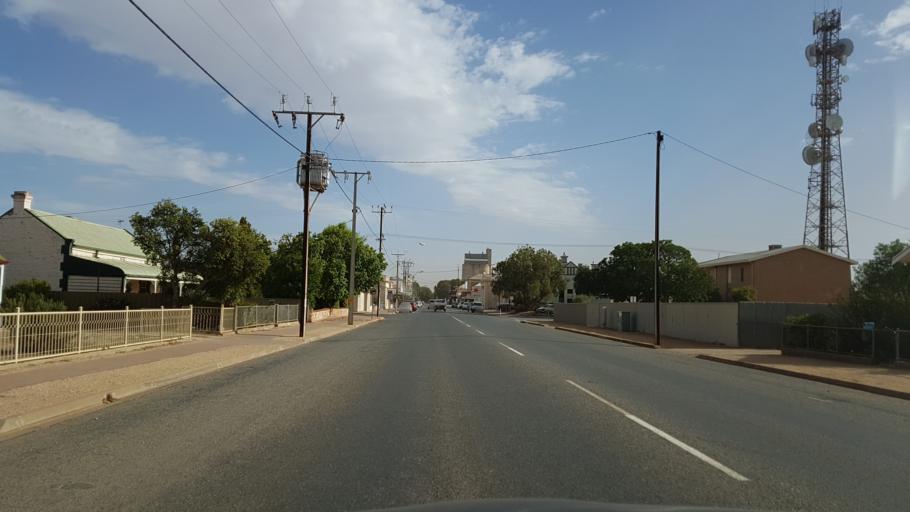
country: AU
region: South Australia
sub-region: Wakefield
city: Balaklava
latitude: -34.1482
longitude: 138.4159
